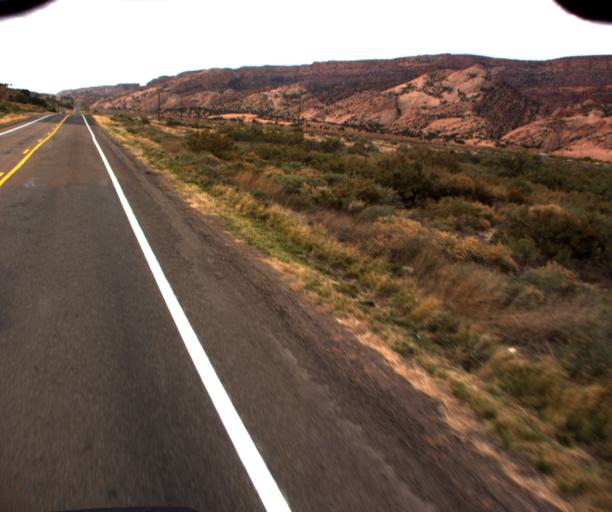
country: US
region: Arizona
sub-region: Navajo County
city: Kayenta
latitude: 36.6757
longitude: -110.3951
